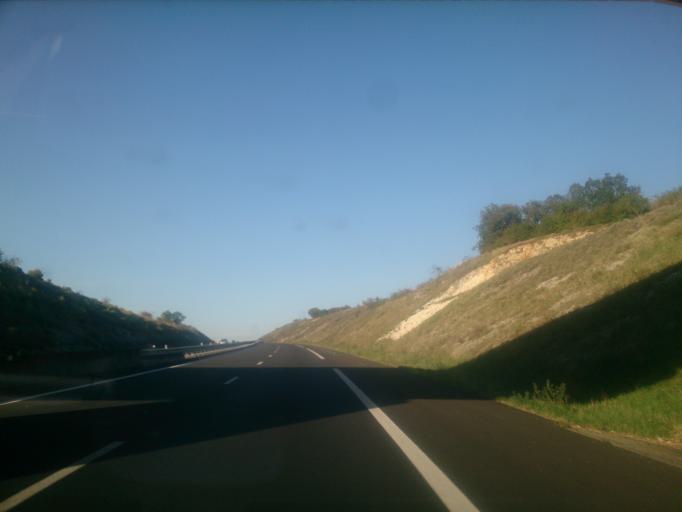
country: FR
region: Midi-Pyrenees
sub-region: Departement du Lot
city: Le Vigan
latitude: 44.6286
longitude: 1.5179
